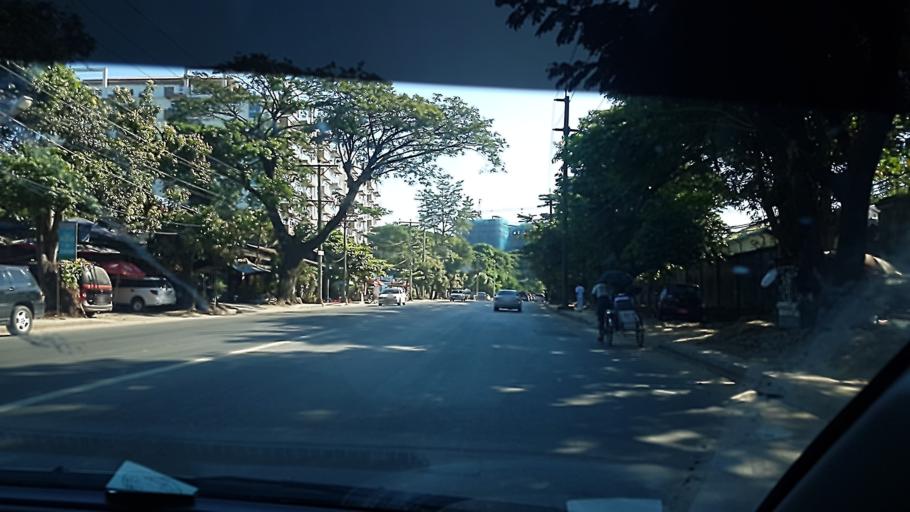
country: MM
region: Yangon
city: Yangon
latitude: 16.8577
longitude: 96.1258
